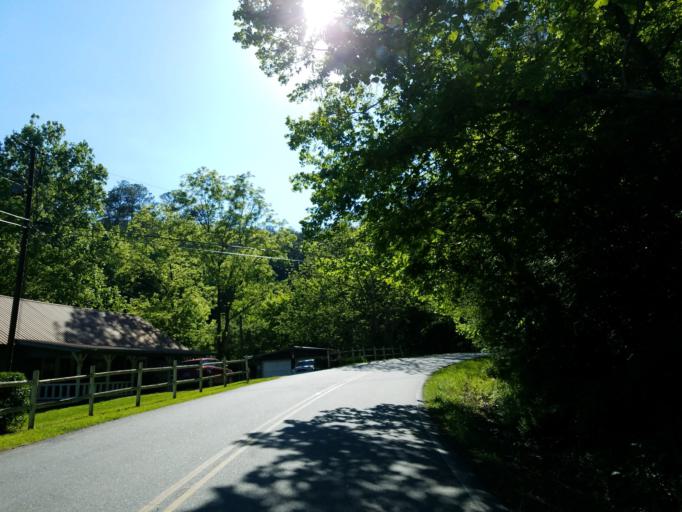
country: US
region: Georgia
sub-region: Pickens County
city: Jasper
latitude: 34.5656
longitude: -84.5122
